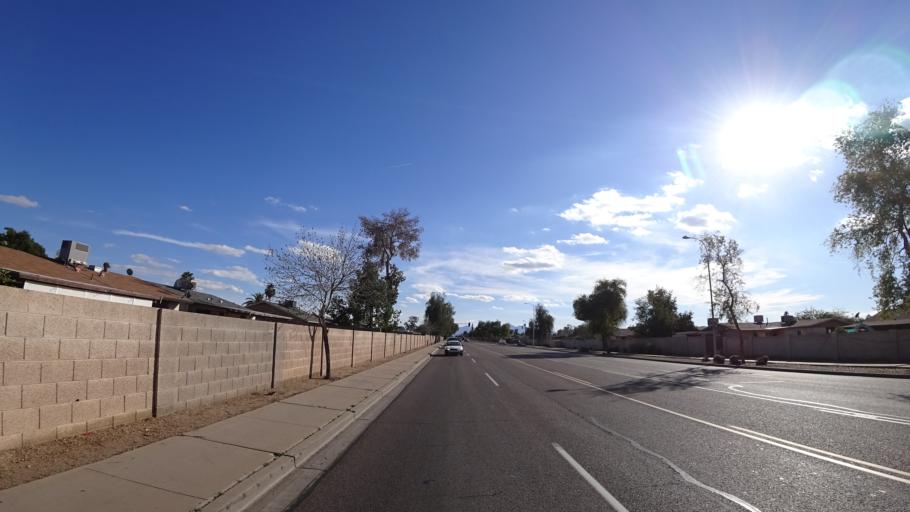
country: US
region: Arizona
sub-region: Maricopa County
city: Tolleson
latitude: 33.4990
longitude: -112.2377
